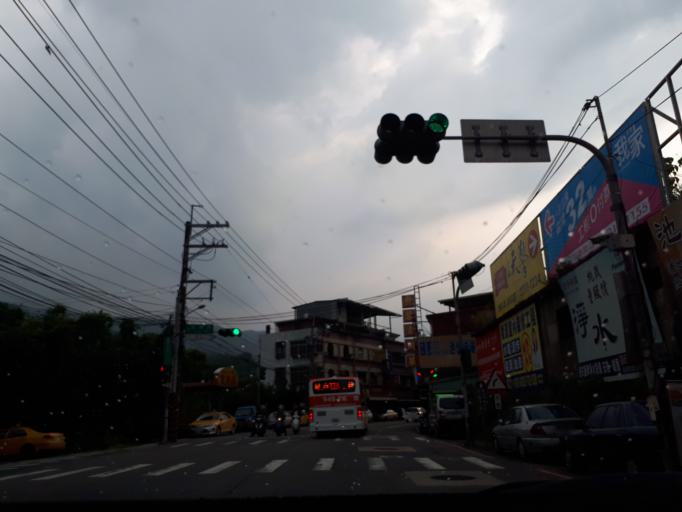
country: TW
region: Taipei
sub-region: Taipei
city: Banqiao
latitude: 24.9525
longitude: 121.4926
